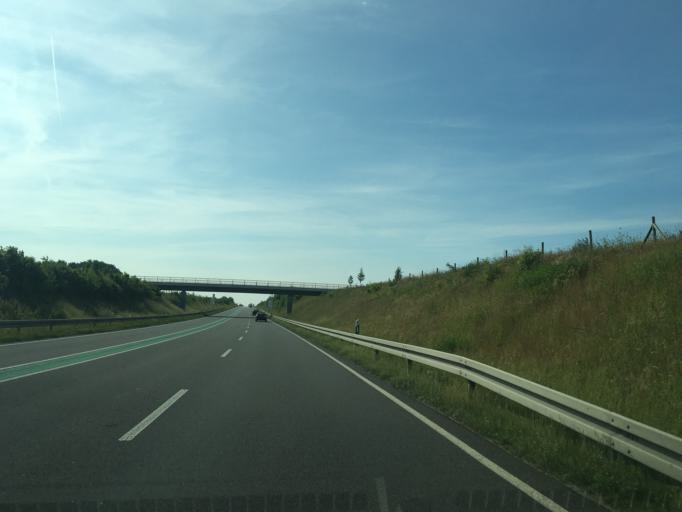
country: DE
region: North Rhine-Westphalia
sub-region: Regierungsbezirk Munster
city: Steinfurt
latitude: 52.1620
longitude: 7.3153
